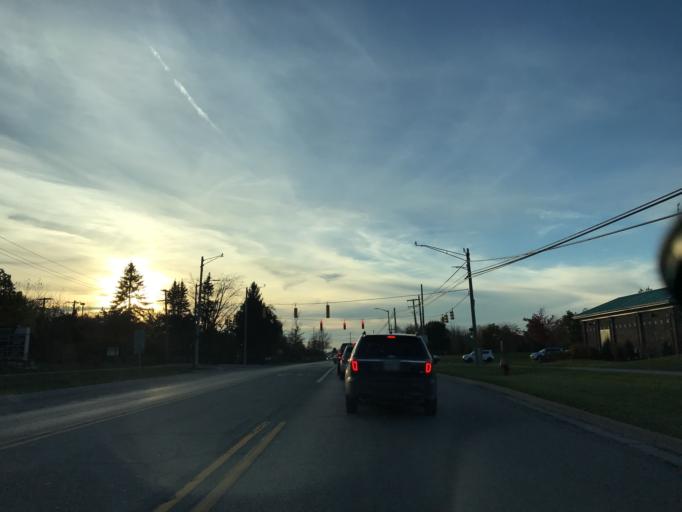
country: US
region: Michigan
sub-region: Oakland County
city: Novi
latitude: 42.4948
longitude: -83.5047
